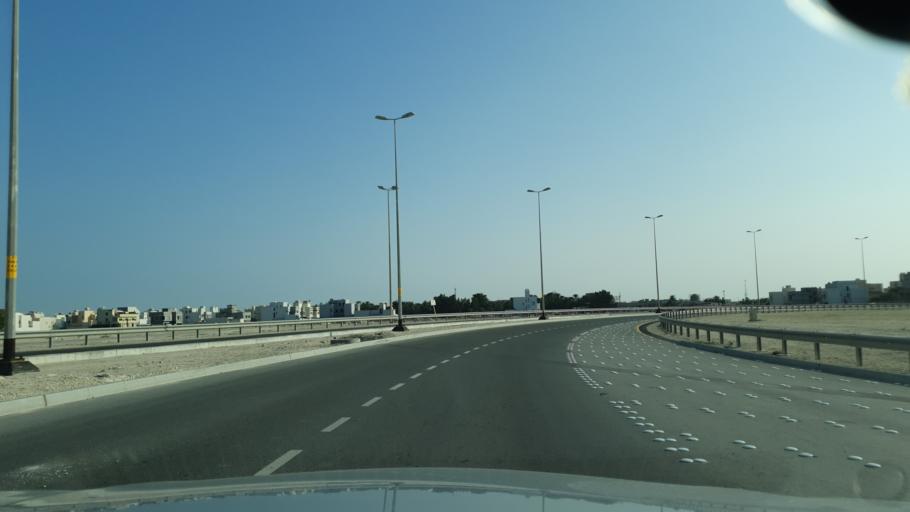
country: BH
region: Manama
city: Jidd Hafs
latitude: 26.2333
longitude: 50.4620
